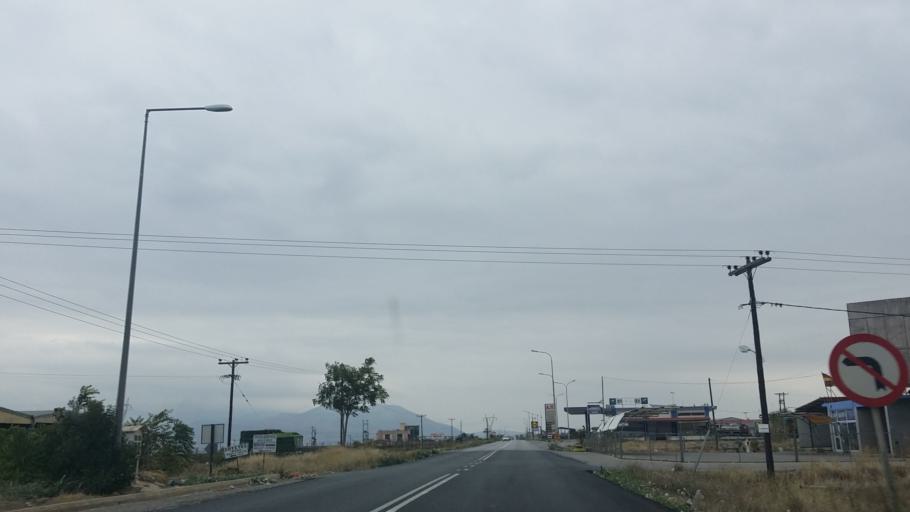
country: GR
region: Central Greece
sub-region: Nomos Voiotias
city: Thivai
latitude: 38.3327
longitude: 23.3082
